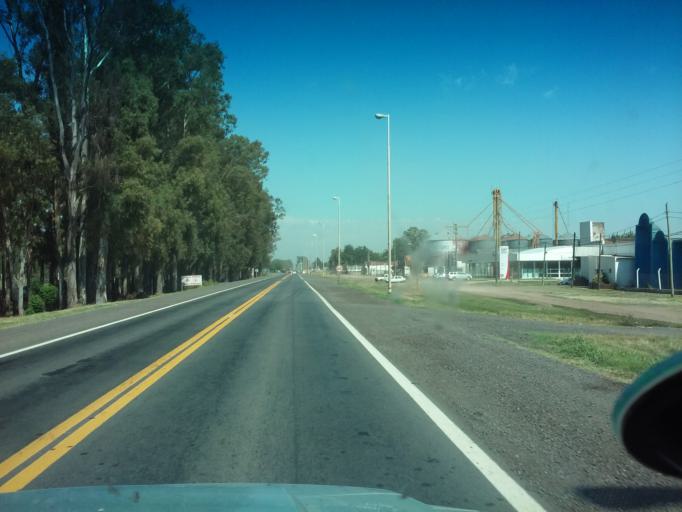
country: AR
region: Buenos Aires
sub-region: Partido de Nueve de Julio
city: Nueve de Julio
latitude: -35.4717
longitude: -60.8566
